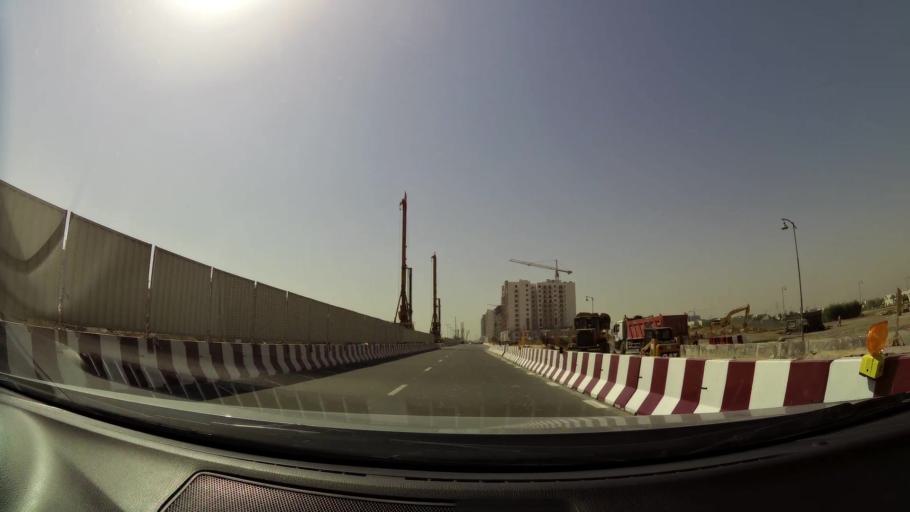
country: AE
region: Dubai
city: Dubai
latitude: 25.0311
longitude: 55.1512
